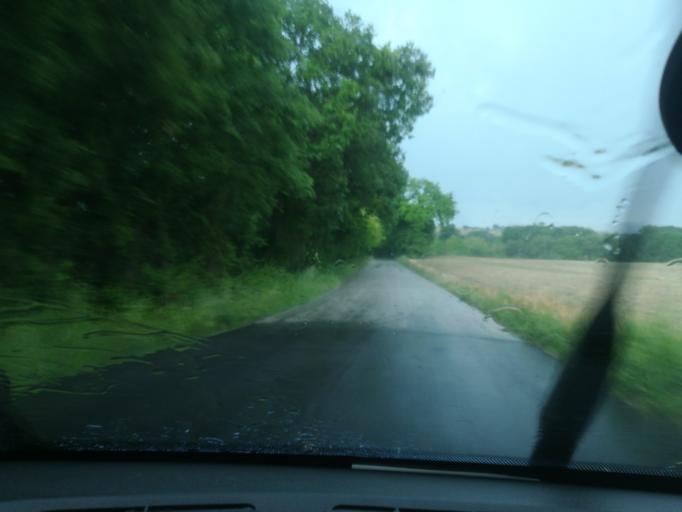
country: IT
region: The Marches
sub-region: Provincia di Macerata
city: Passo di Treia
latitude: 43.3087
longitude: 13.3360
